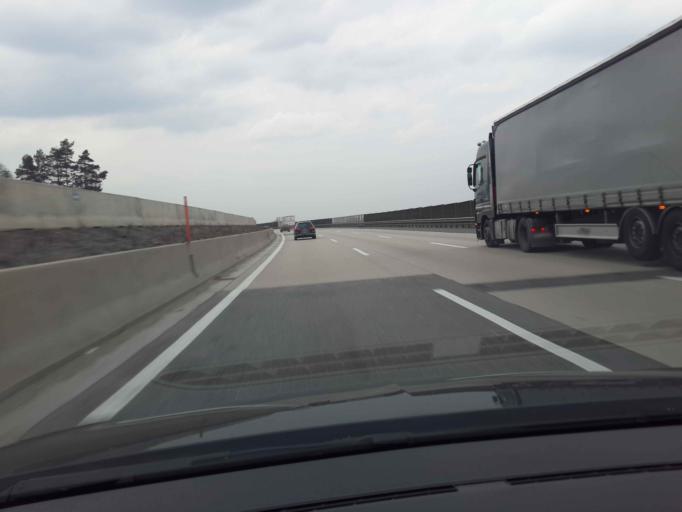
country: AT
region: Lower Austria
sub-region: Politischer Bezirk Sankt Polten
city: Neulengbach
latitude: 48.1736
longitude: 15.8685
